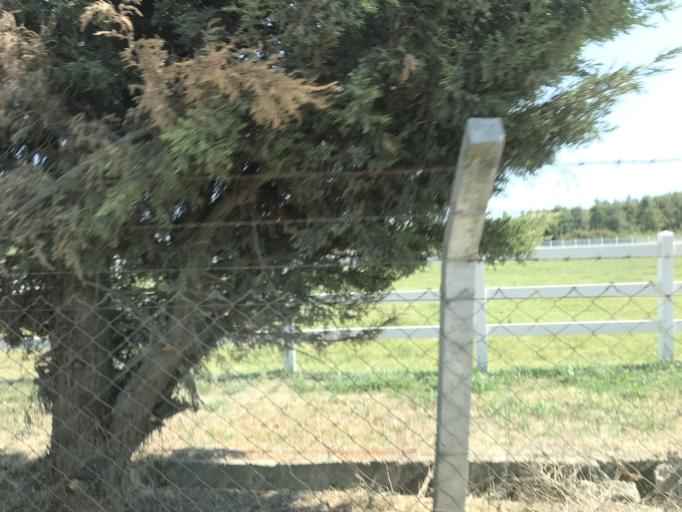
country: TR
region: Izmir
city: Urla
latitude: 38.2878
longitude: 26.7195
